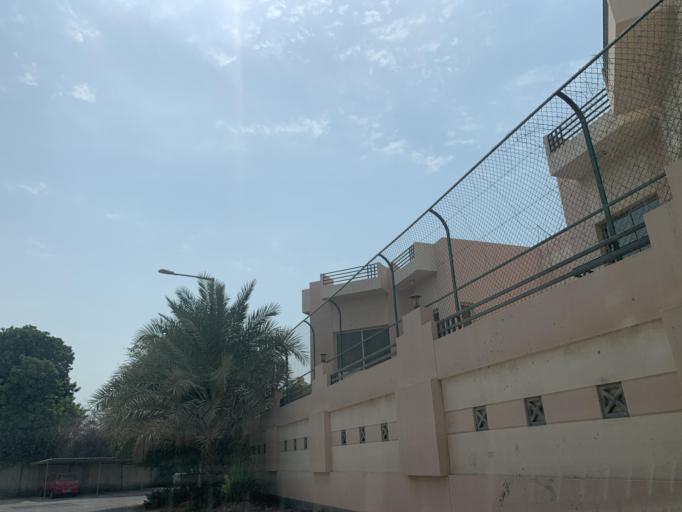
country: BH
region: Manama
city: Jidd Hafs
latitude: 26.2112
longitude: 50.4856
